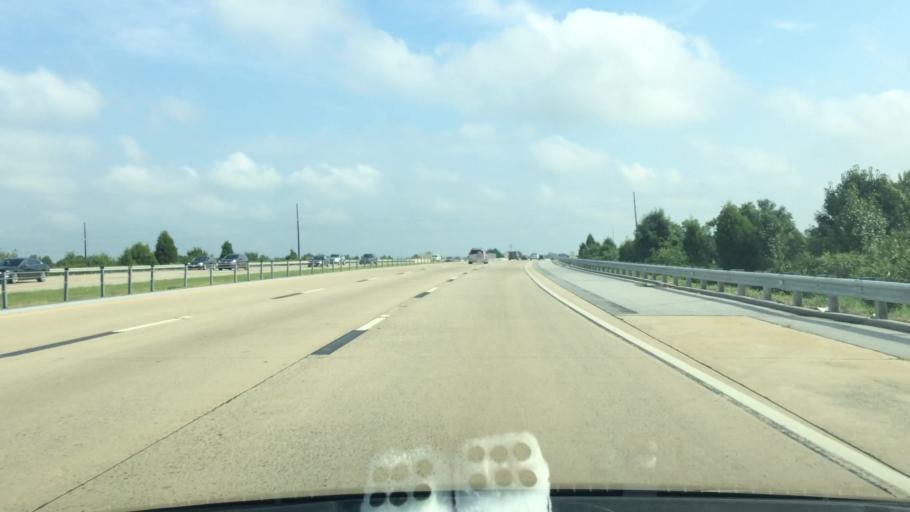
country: US
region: Delaware
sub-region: New Castle County
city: Bear
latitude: 39.5874
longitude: -75.6615
